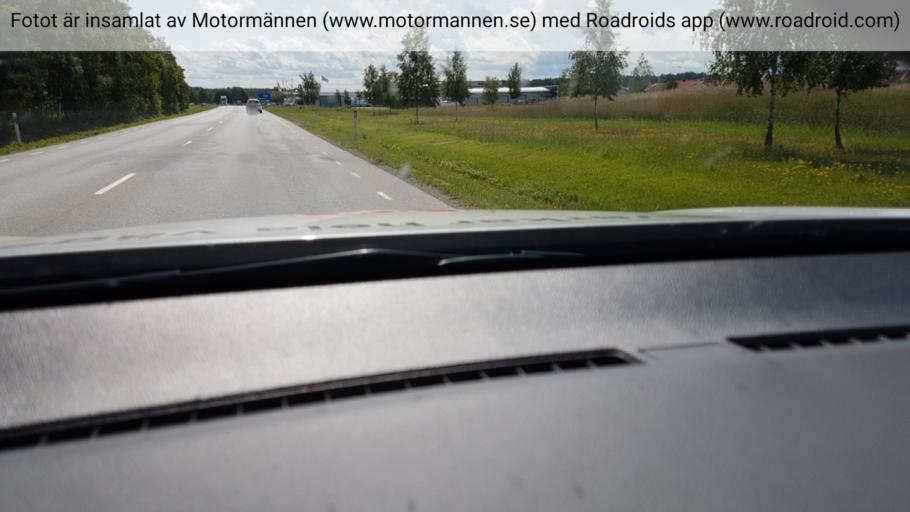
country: SE
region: Vaestra Goetaland
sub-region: Lidkopings Kommun
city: Lidkoping
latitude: 58.5077
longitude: 13.1210
